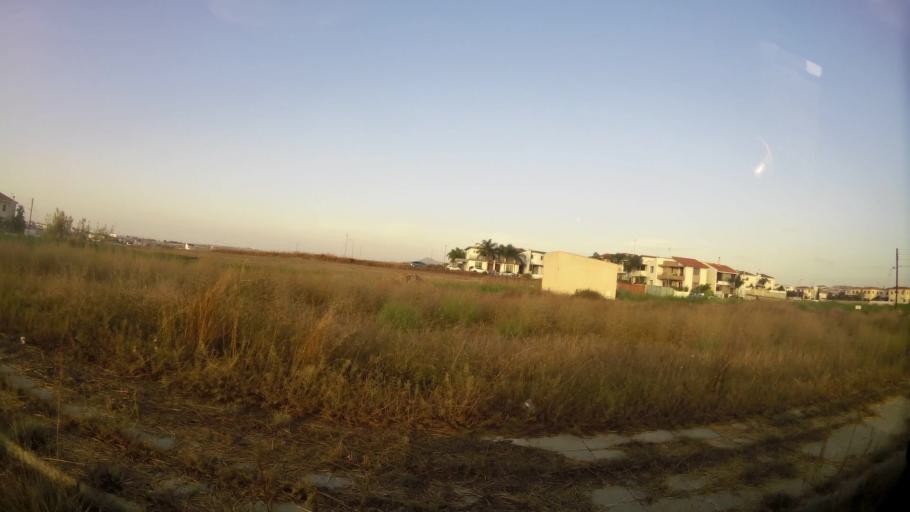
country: CY
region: Larnaka
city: Aradippou
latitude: 34.9222
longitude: 33.5881
